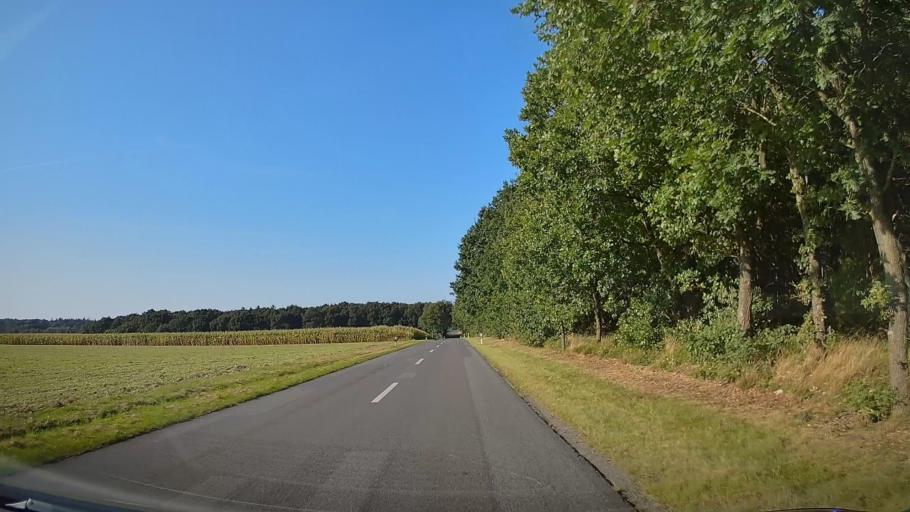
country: DE
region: Lower Saxony
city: Nordholz
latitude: 53.8099
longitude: 8.5997
